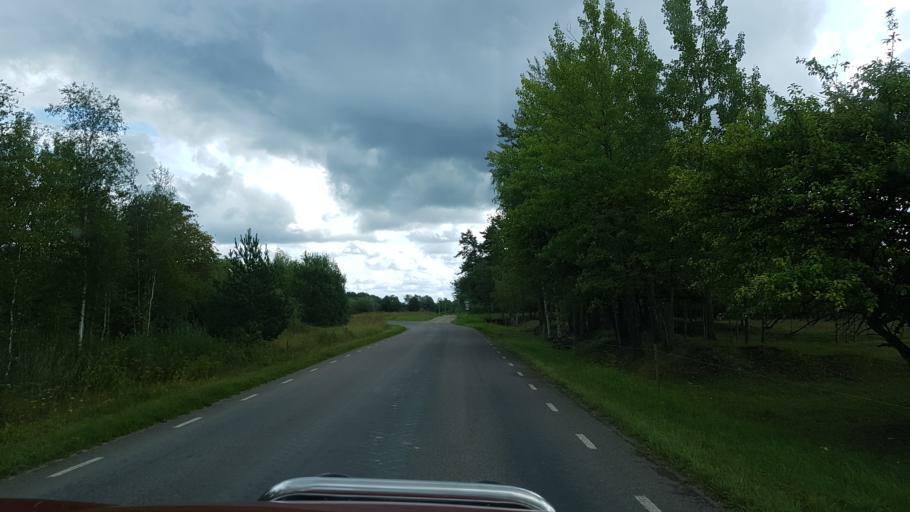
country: EE
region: Laeaene
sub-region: Lihula vald
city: Lihula
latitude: 58.7225
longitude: 23.9581
